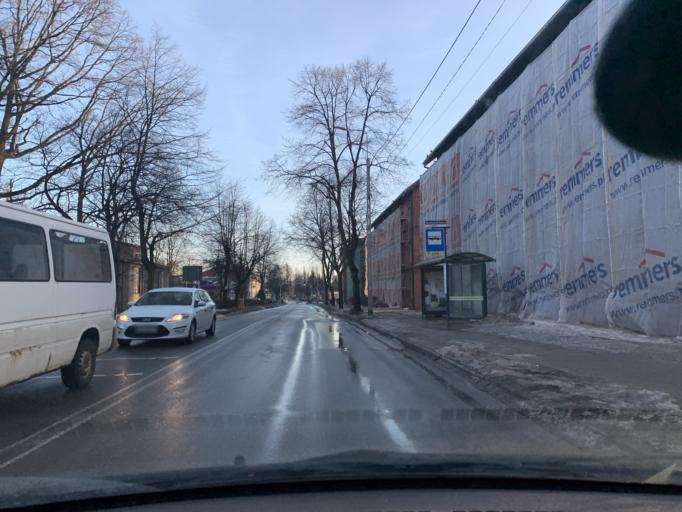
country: PL
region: Silesian Voivodeship
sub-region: Powiat tarnogorski
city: Radzionkow
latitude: 50.3873
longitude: 18.8990
